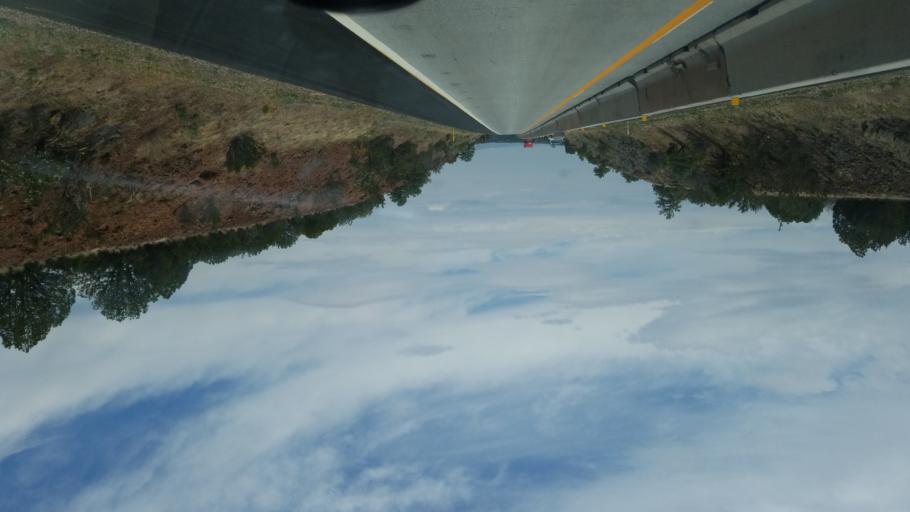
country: US
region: Arizona
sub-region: Coconino County
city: Williams
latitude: 35.2224
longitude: -112.2510
